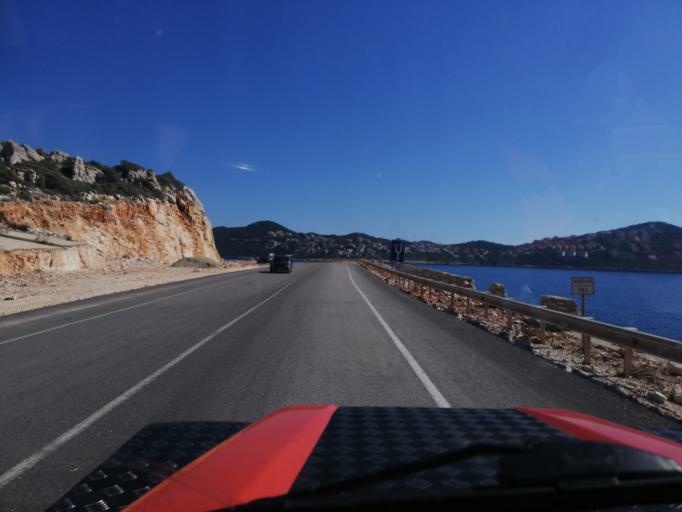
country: TR
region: Antalya
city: Kas
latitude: 36.2021
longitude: 29.5844
